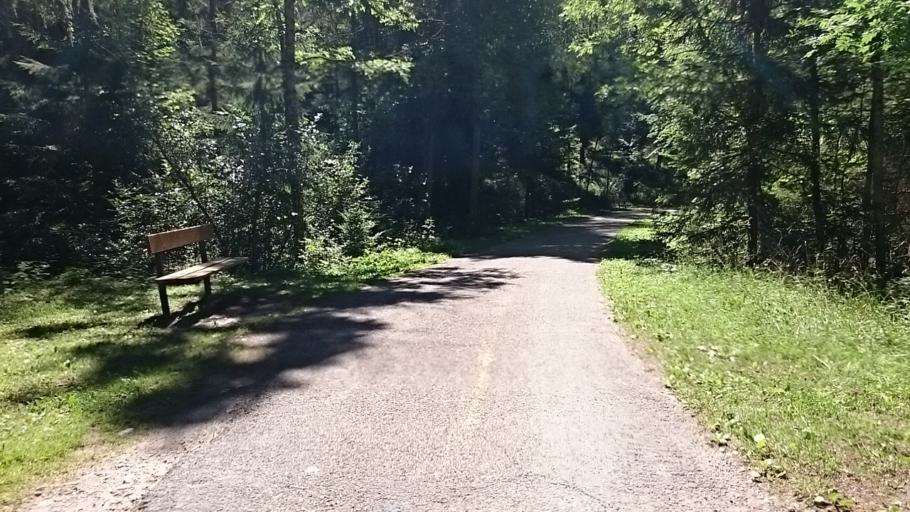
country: IT
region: Veneto
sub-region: Provincia di Belluno
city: Cortina d'Ampezzo
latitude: 46.5588
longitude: 12.1276
